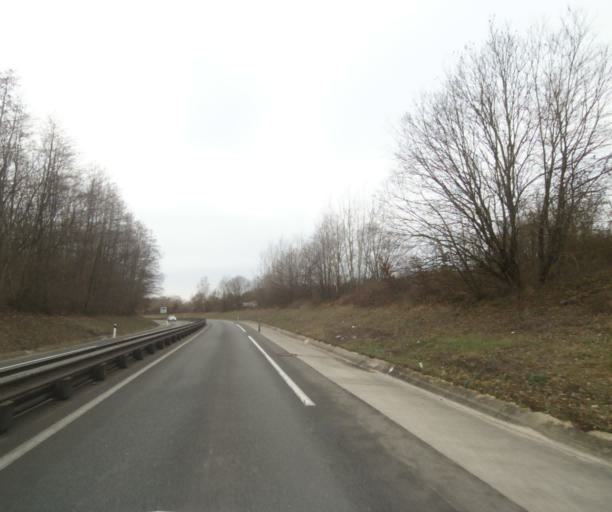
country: FR
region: Lorraine
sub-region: Departement de la Meuse
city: Ancerville
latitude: 48.6224
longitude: 4.9910
